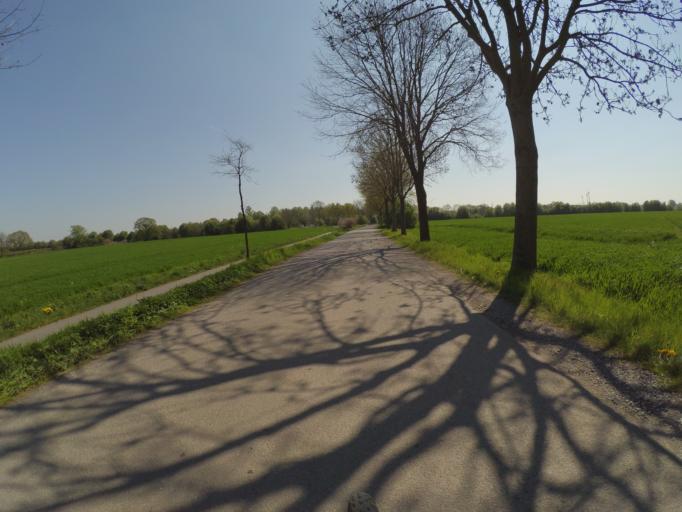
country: DE
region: North Rhine-Westphalia
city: Ludinghausen
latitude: 51.7444
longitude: 7.4611
